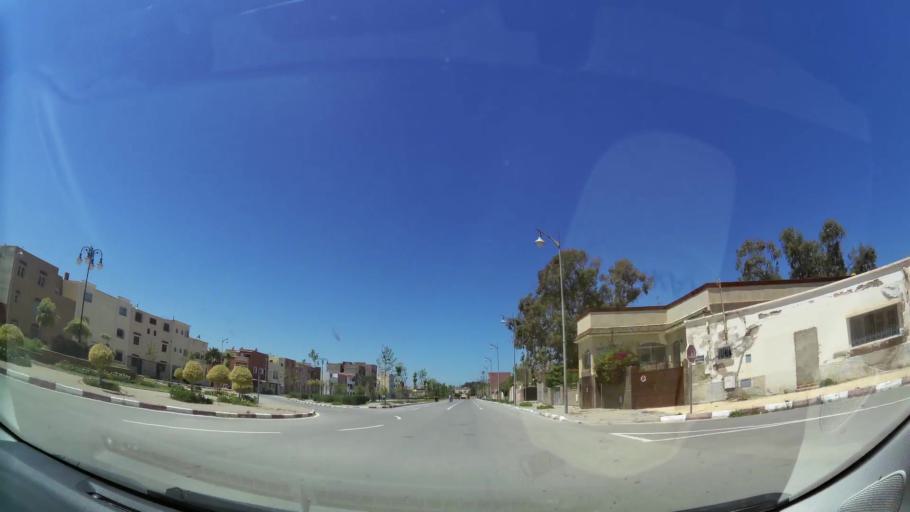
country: MA
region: Oriental
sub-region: Berkane-Taourirt
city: Madagh
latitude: 35.0847
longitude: -2.2284
